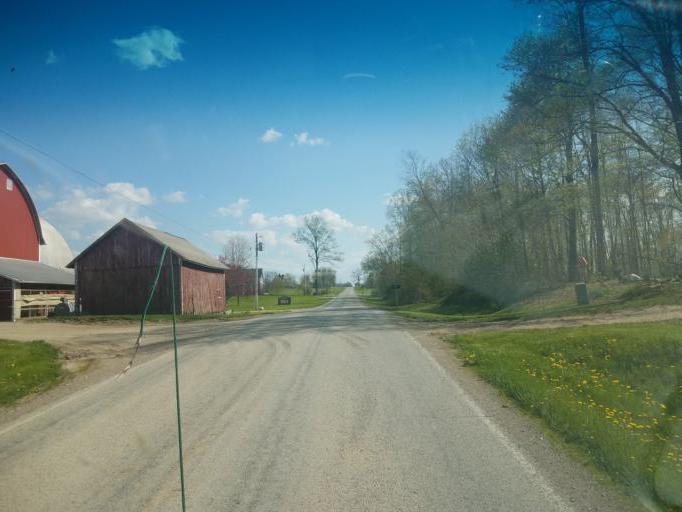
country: US
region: Ohio
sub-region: Medina County
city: Westfield Center
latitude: 40.9662
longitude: -81.9576
